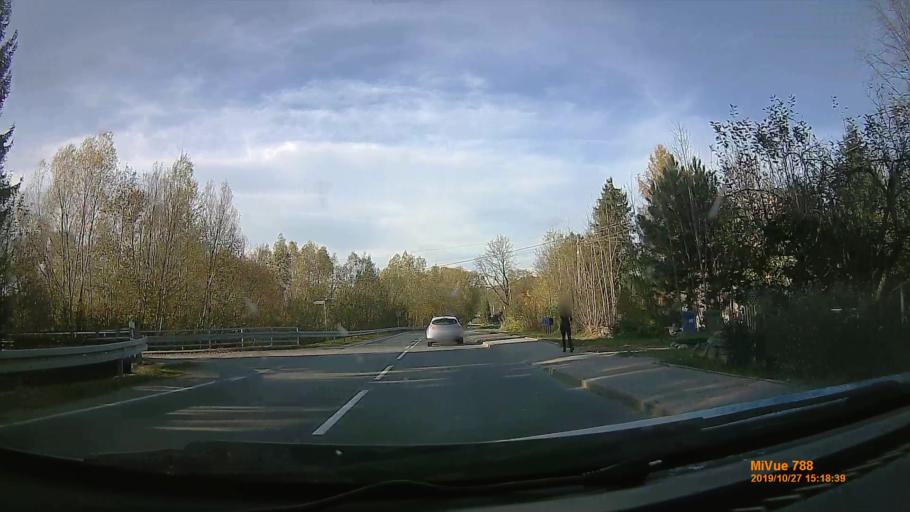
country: PL
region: Lower Silesian Voivodeship
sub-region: Powiat klodzki
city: Bystrzyca Klodzka
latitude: 50.2686
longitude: 16.6592
